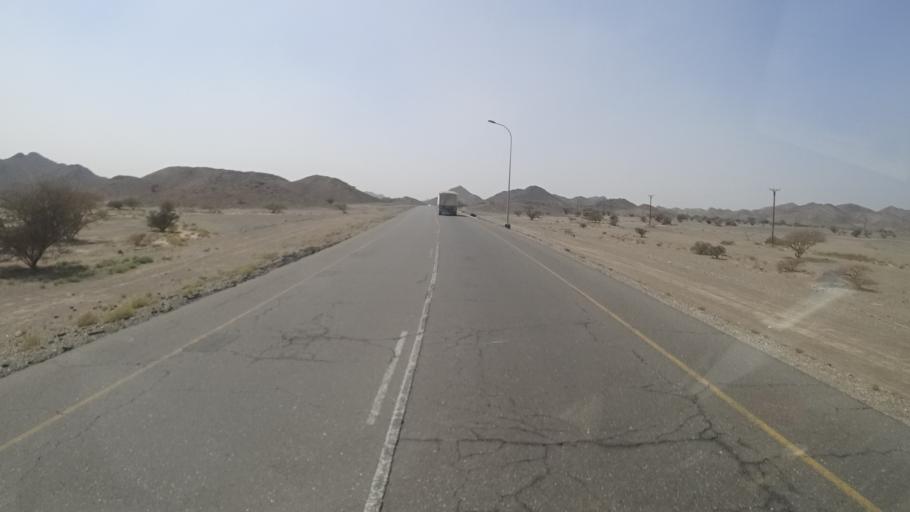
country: OM
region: Ash Sharqiyah
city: Ibra'
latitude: 22.6201
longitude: 58.3656
